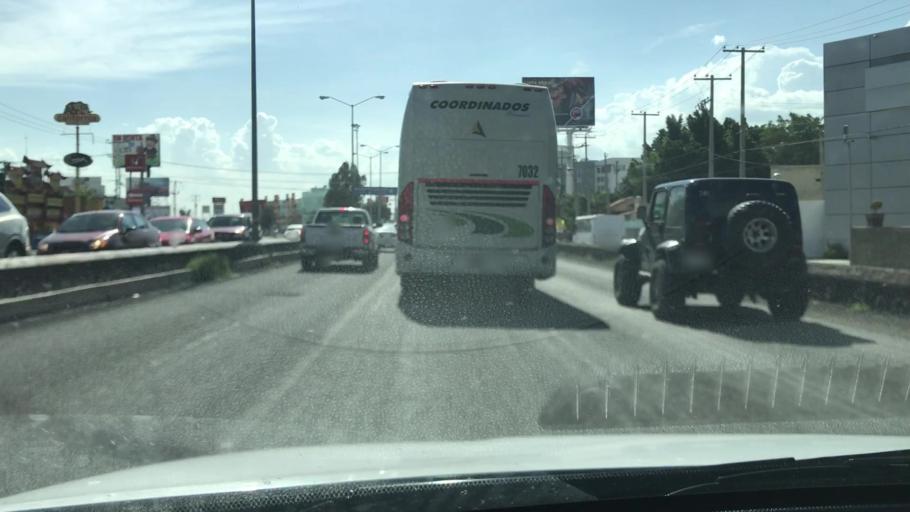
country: MX
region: Guanajuato
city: Celaya
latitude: 20.5172
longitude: -100.7875
